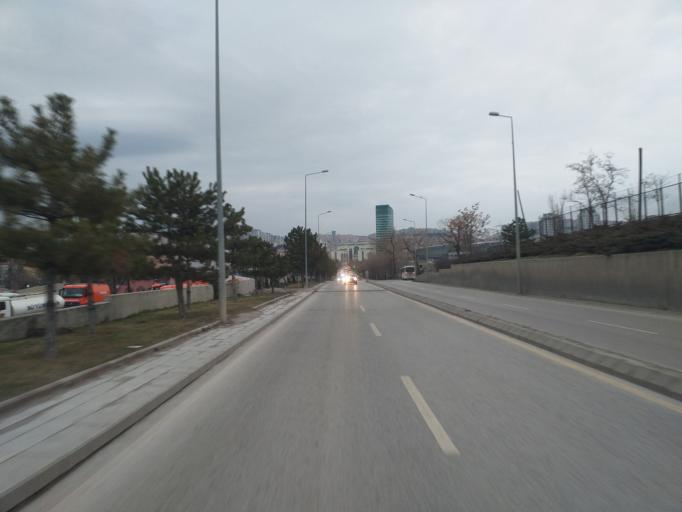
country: TR
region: Ankara
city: Ankara
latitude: 39.9624
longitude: 32.8215
